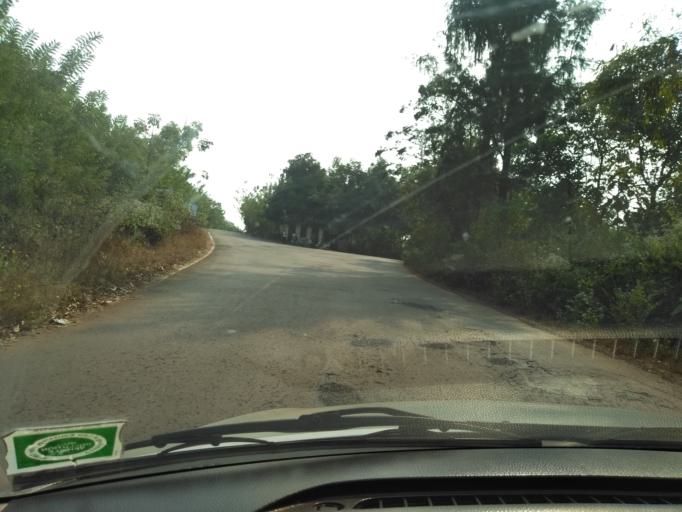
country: IN
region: Maharashtra
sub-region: Sindhudurg
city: Savantvadi
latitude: 15.8114
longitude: 73.9053
